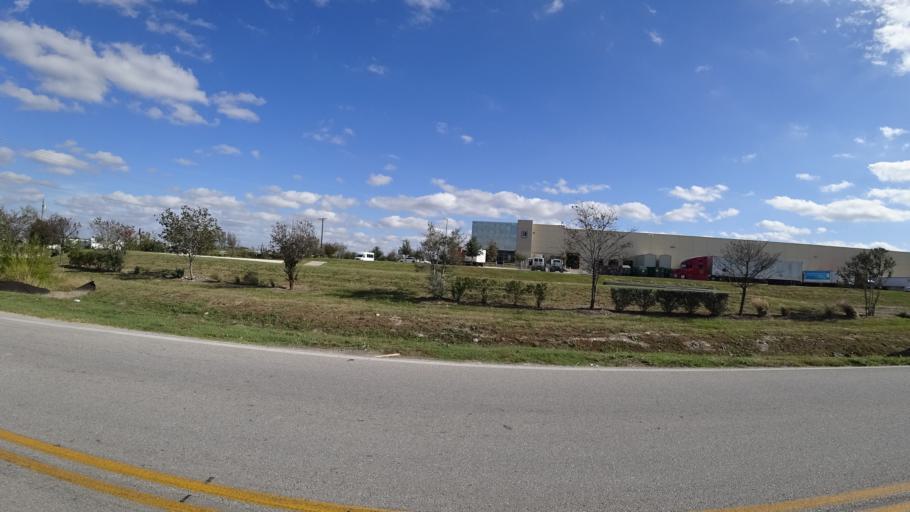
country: US
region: Texas
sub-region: Travis County
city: Wells Branch
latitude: 30.4644
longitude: -97.6734
